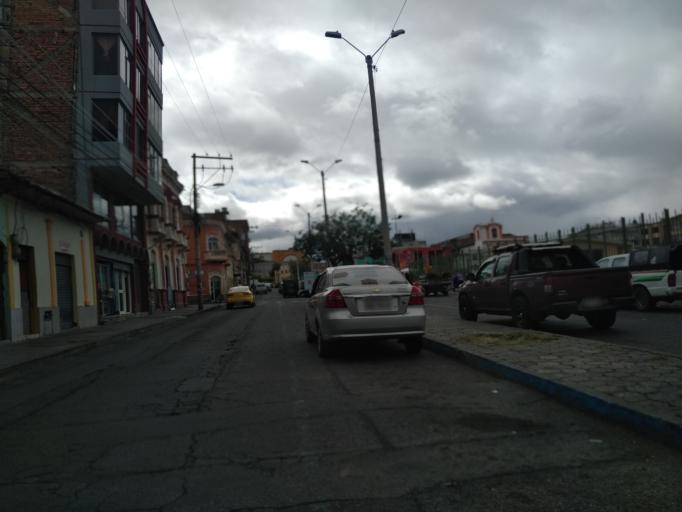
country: EC
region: Chimborazo
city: Riobamba
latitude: -1.6703
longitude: -78.6539
